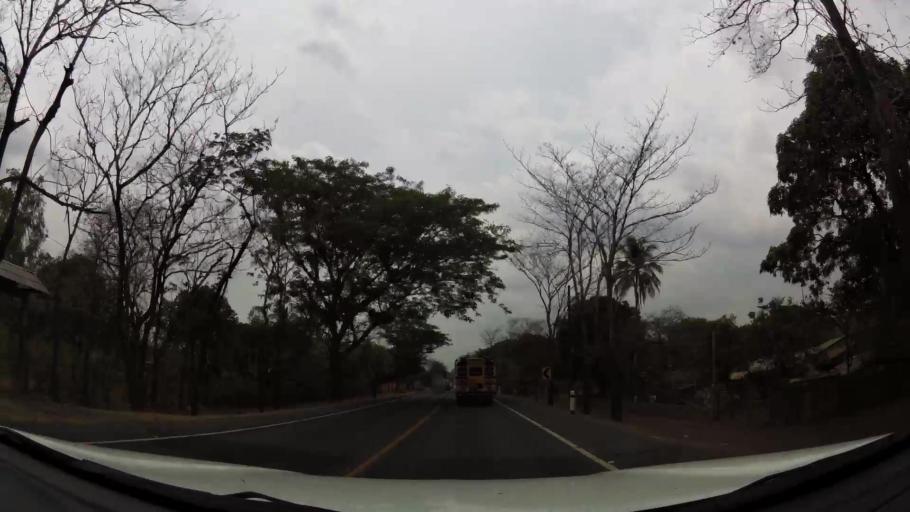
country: NI
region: Leon
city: Telica
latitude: 12.5135
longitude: -86.8619
